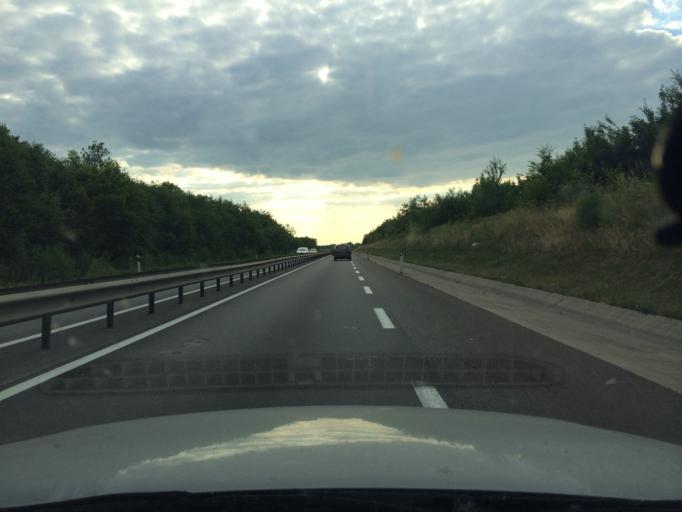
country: FR
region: Champagne-Ardenne
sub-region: Departement de la Haute-Marne
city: Bettancourt-la-Ferree
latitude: 48.6207
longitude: 4.9767
